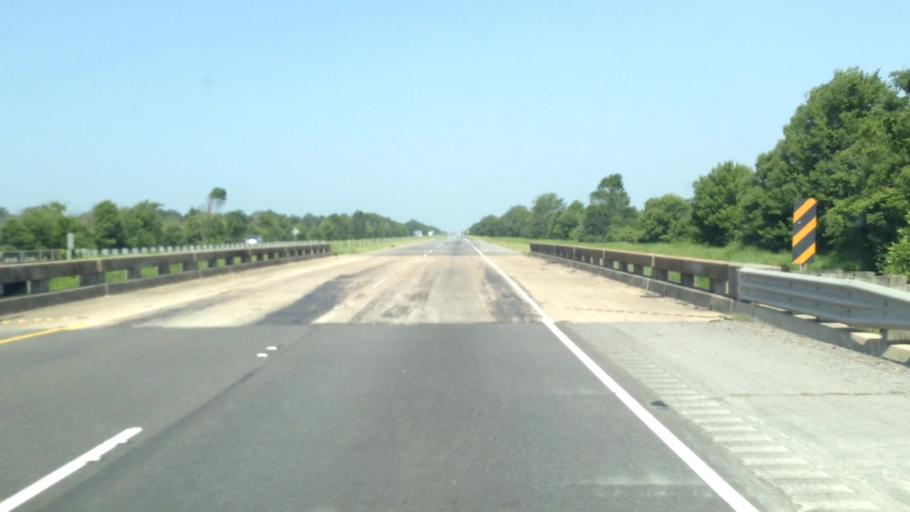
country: US
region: Louisiana
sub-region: Madison Parish
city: Tallulah
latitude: 32.4066
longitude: -91.2340
